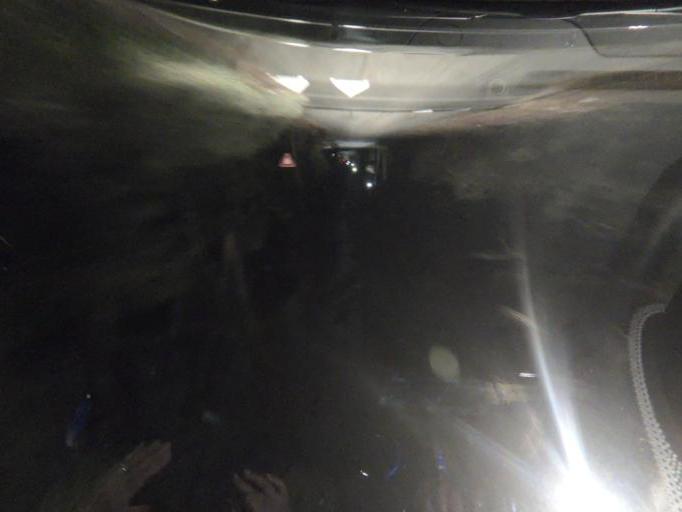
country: US
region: Georgia
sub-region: Fulton County
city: East Point
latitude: 33.7131
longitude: -84.4865
